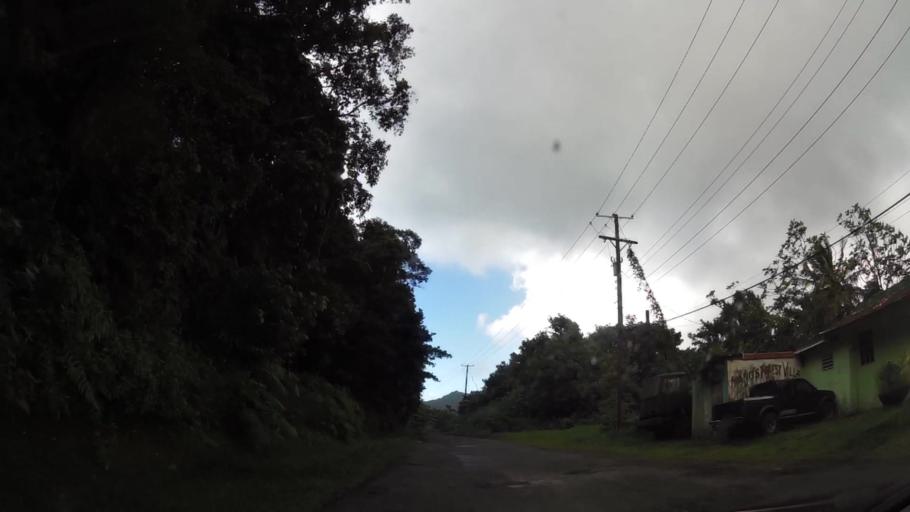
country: DM
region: Saint Paul
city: Pont Casse
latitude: 15.3920
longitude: -61.3155
